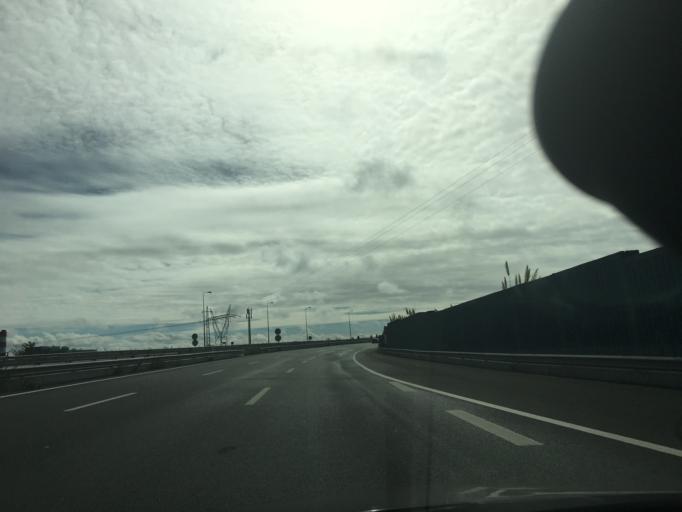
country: PT
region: Porto
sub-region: Matosinhos
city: Santa Cruz do Bispo
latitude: 41.2331
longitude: -8.6538
